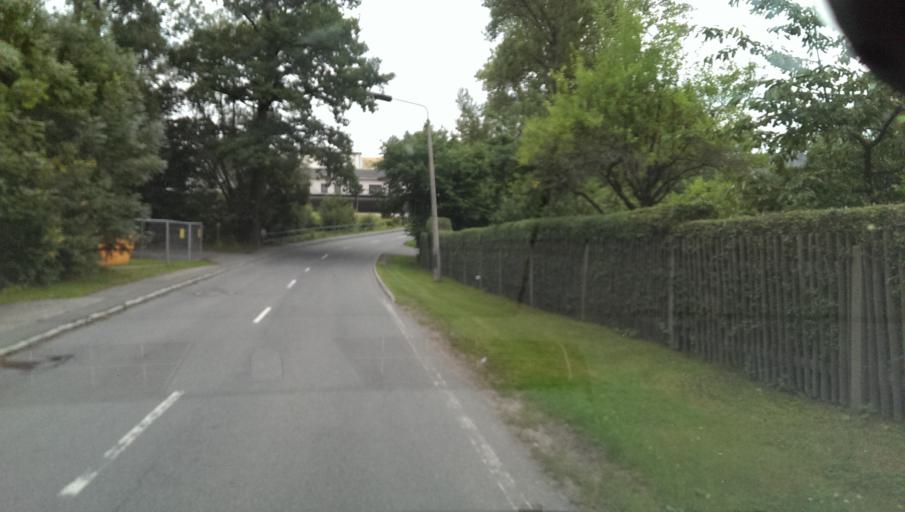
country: DE
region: Thuringia
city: Zeulenroda
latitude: 50.6503
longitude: 11.9695
